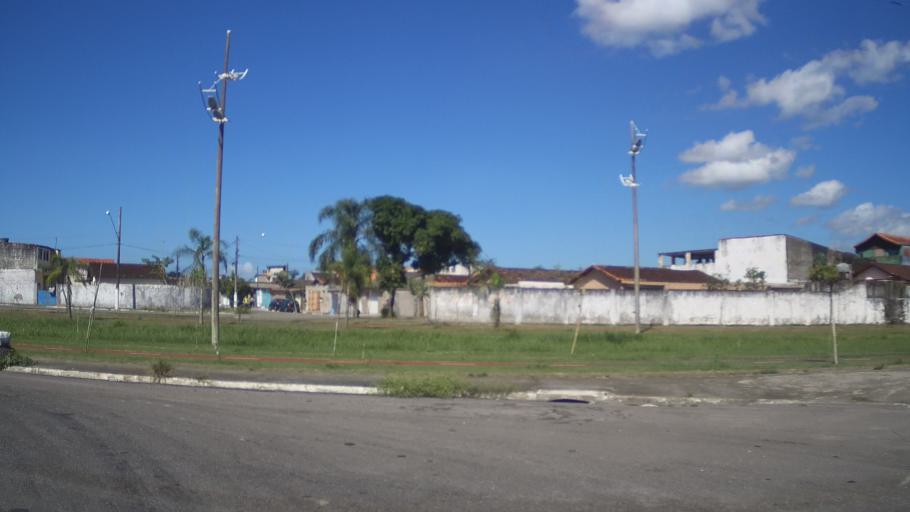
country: BR
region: Sao Paulo
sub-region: Mongagua
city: Mongagua
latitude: -24.0288
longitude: -46.5333
